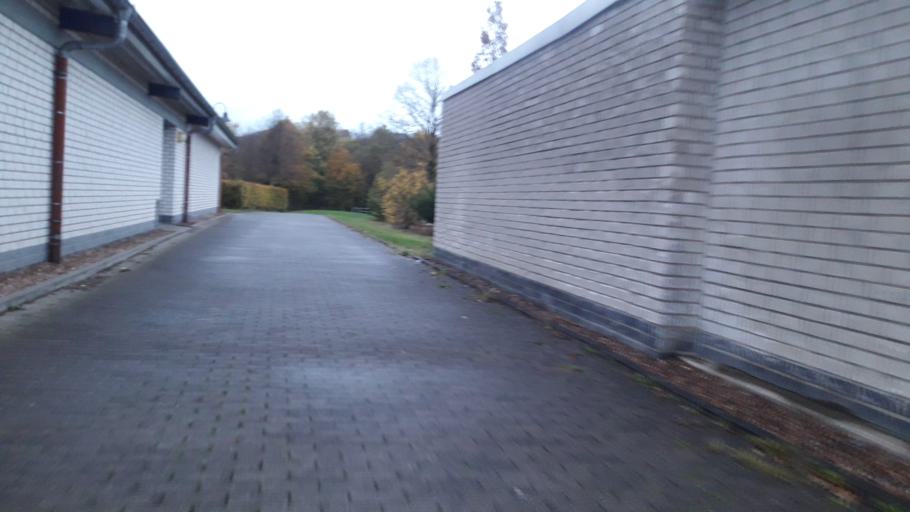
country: DE
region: North Rhine-Westphalia
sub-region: Regierungsbezirk Detmold
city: Altenbeken
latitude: 51.7591
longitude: 8.9440
